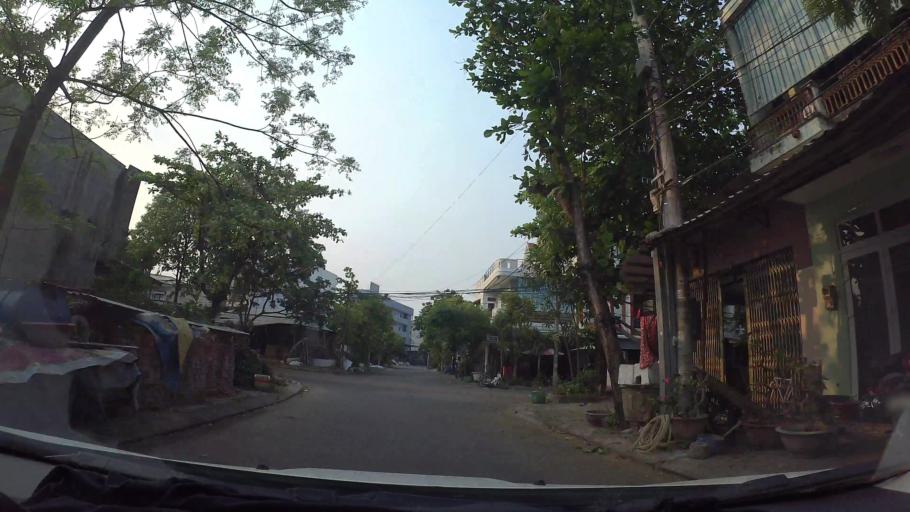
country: VN
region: Da Nang
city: Cam Le
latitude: 16.0191
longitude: 108.1968
